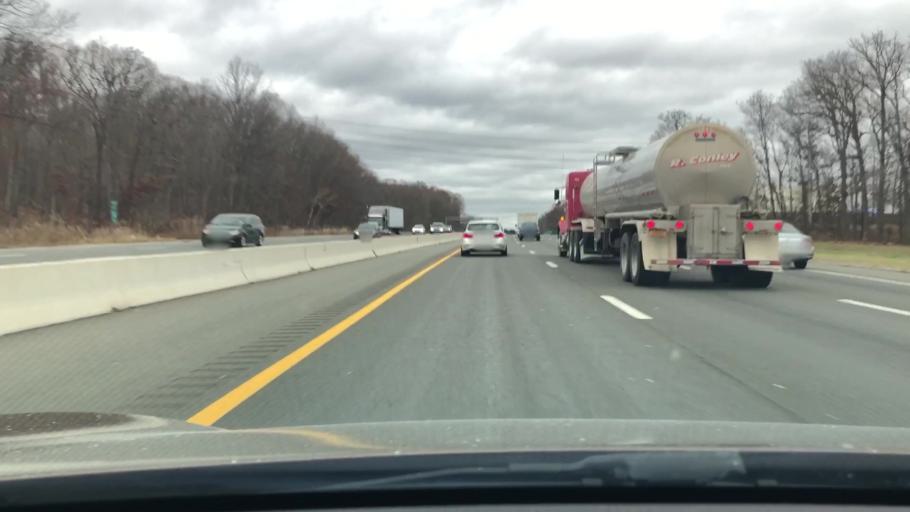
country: US
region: New Jersey
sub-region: Morris County
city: Wharton
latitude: 40.9104
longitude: -74.5620
